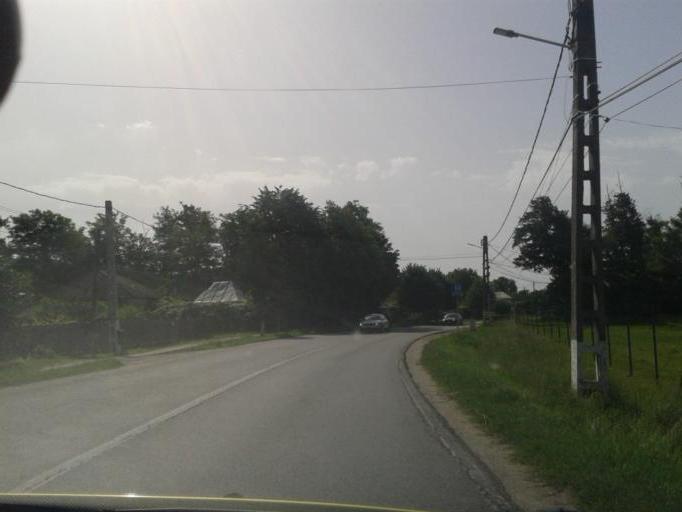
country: RO
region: Valcea
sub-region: Comuna Bunesti
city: Bunesti
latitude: 45.1064
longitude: 24.2002
